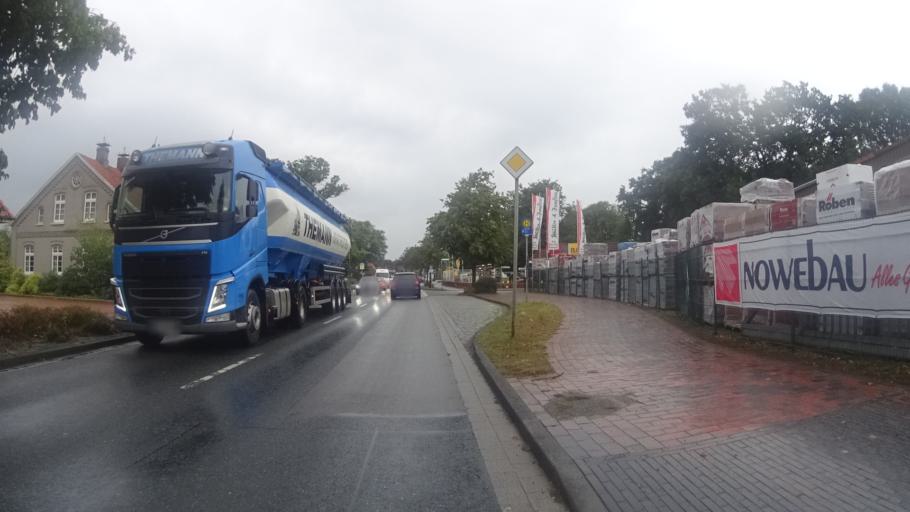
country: DE
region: Lower Saxony
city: Hesel
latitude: 53.3039
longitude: 7.5942
